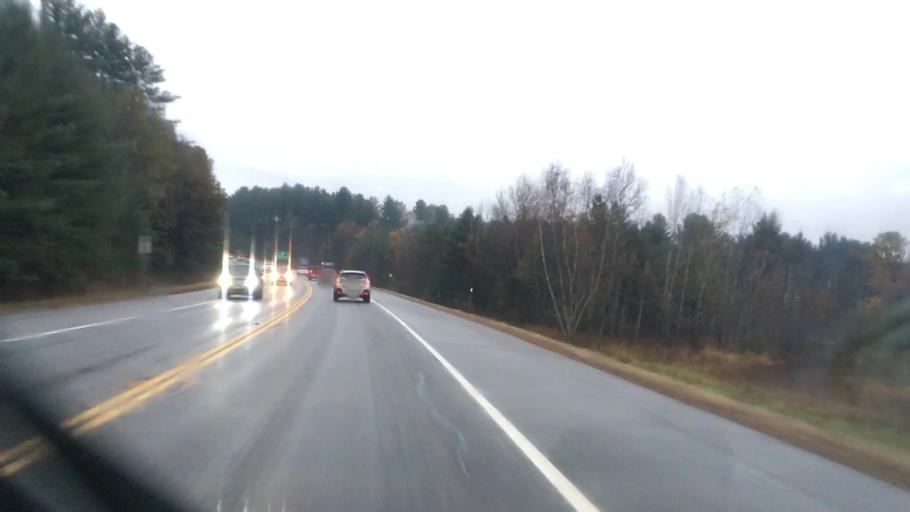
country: US
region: New Hampshire
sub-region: Hillsborough County
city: Milford
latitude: 42.8200
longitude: -71.6562
